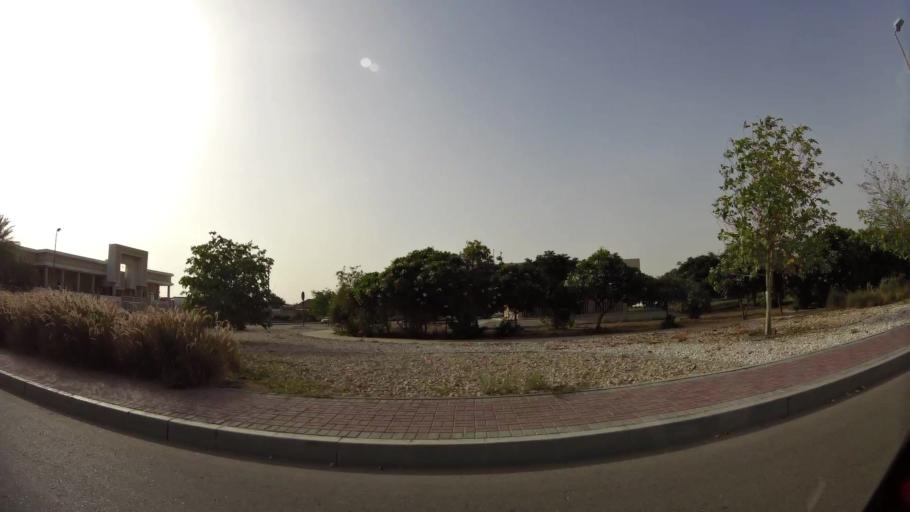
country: AE
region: Abu Dhabi
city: Al Ain
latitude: 24.2140
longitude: 55.6523
